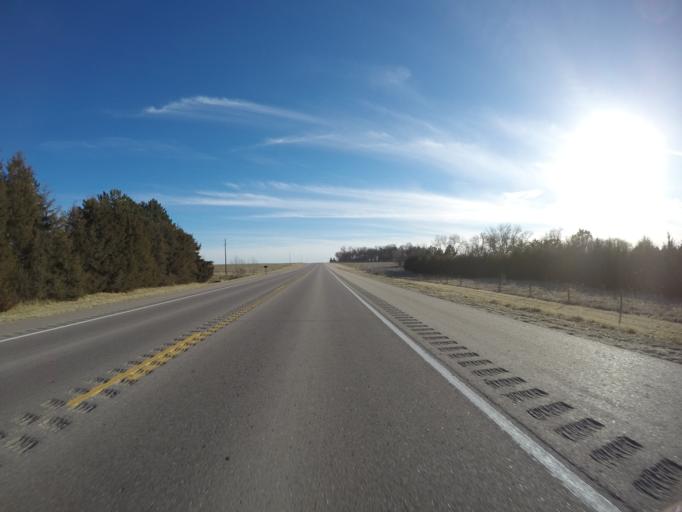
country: US
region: Nebraska
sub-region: Gage County
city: Wymore
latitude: 40.1514
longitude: -96.7469
